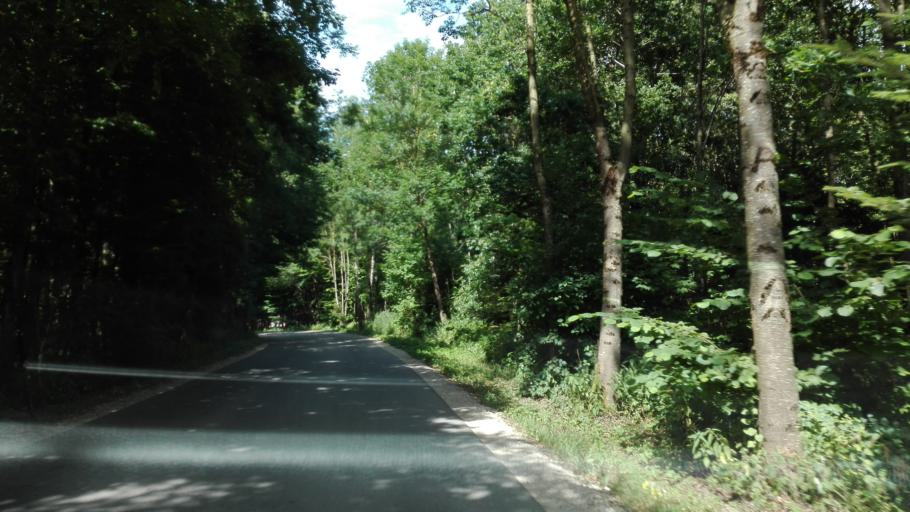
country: AT
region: Upper Austria
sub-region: Politischer Bezirk Grieskirchen
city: Bad Schallerbach
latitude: 48.2292
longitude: 13.9573
